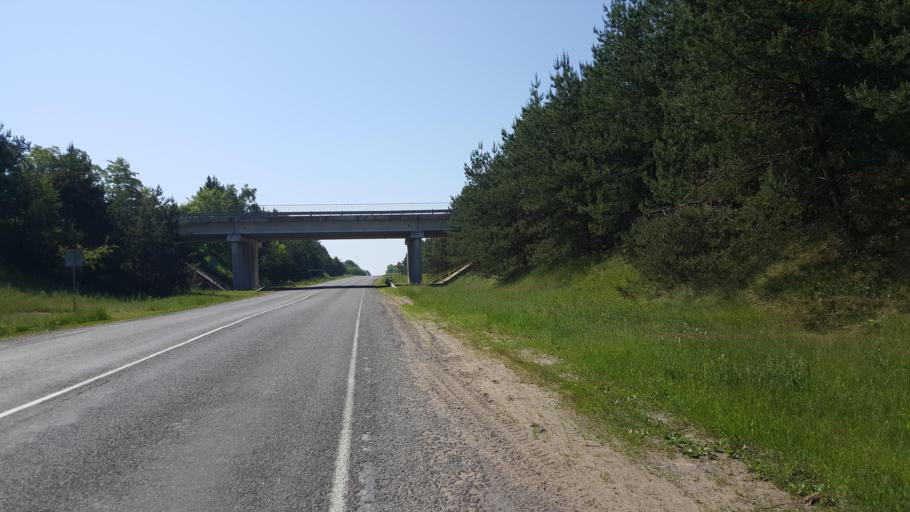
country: BY
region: Brest
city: Kamyanyets
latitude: 52.3428
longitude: 23.9059
